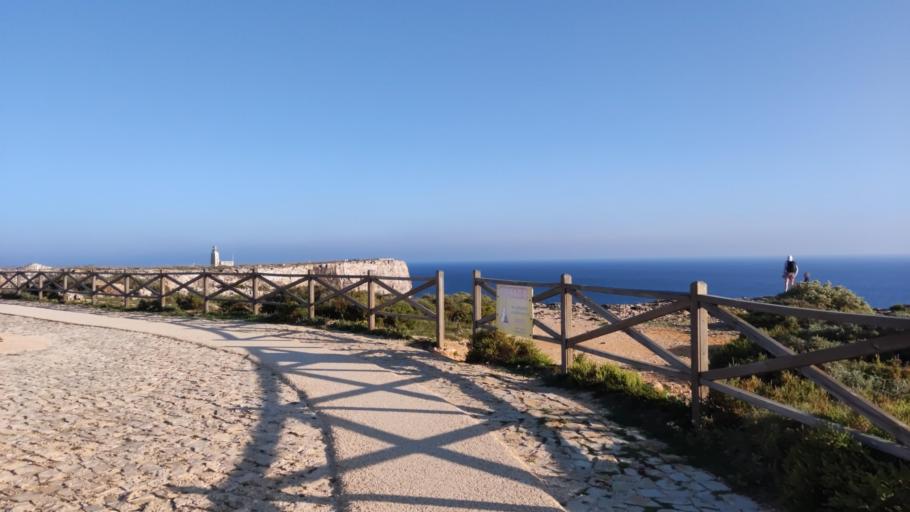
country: PT
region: Faro
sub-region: Vila do Bispo
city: Sagres
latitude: 36.9983
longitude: -8.9515
